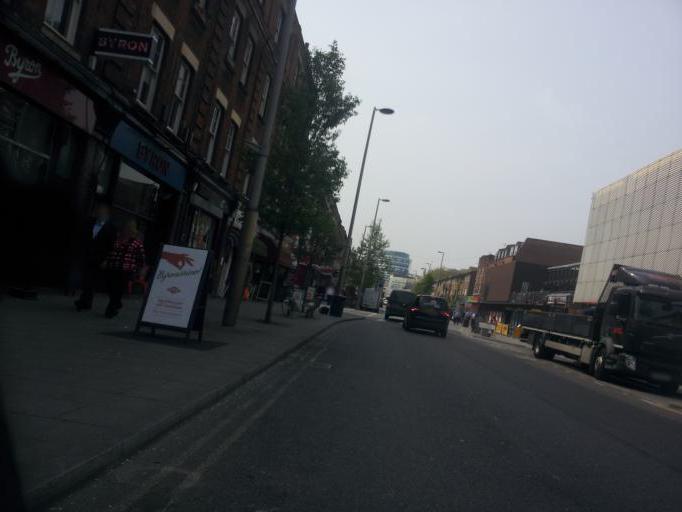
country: GB
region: England
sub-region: Greater London
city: Lambeth
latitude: 51.5033
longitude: -0.1068
